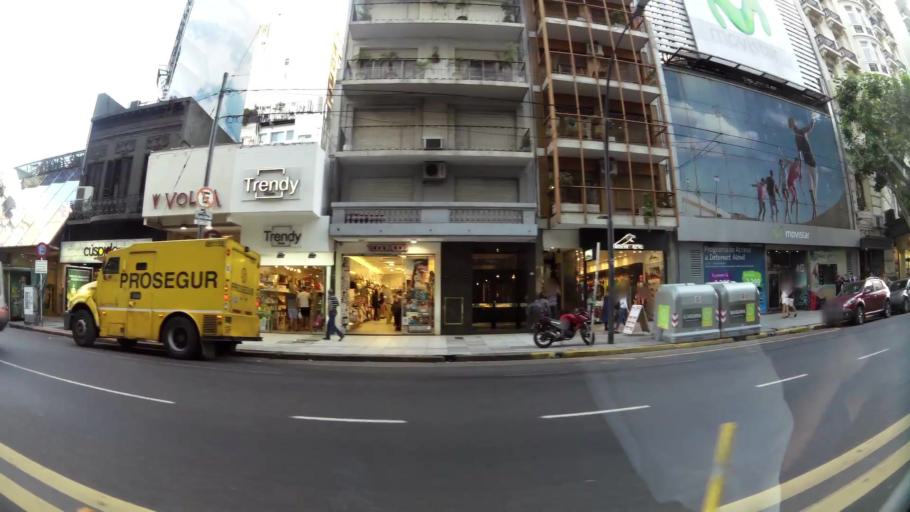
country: AR
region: Buenos Aires F.D.
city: Retiro
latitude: -34.5964
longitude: -58.3941
